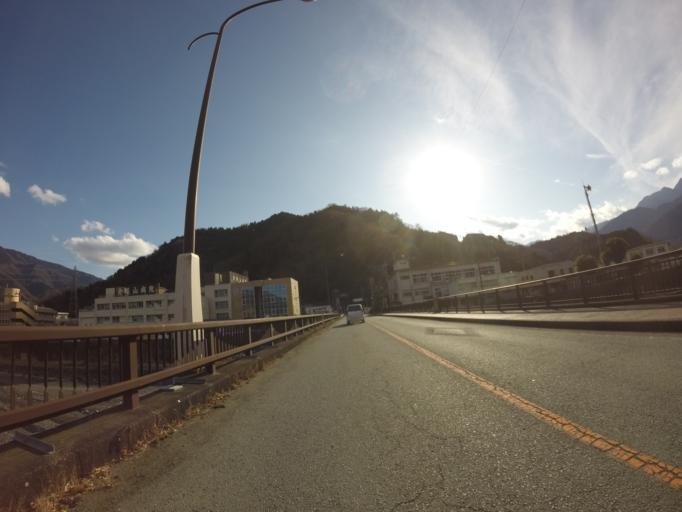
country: JP
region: Shizuoka
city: Fujinomiya
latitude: 35.3715
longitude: 138.4439
